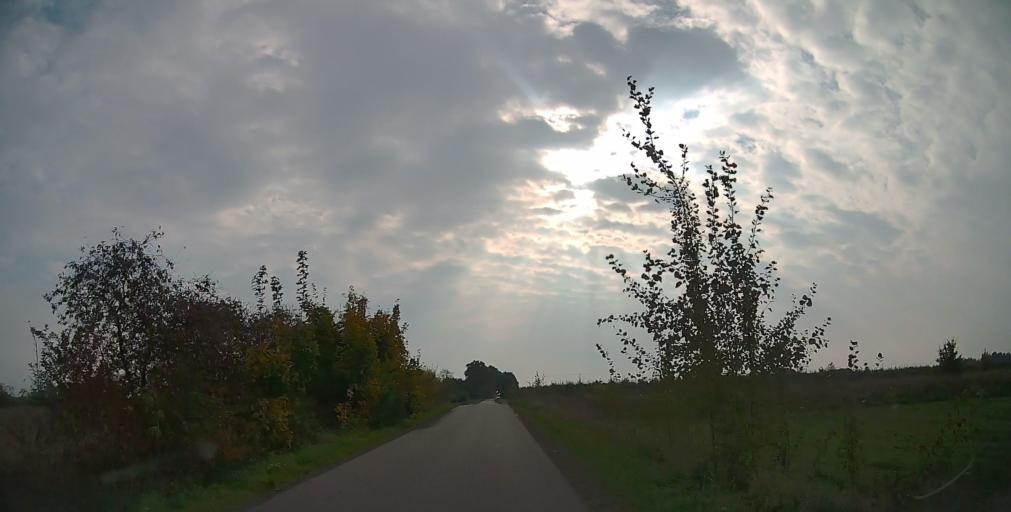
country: PL
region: Masovian Voivodeship
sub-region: Powiat grojecki
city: Mogielnica
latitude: 51.6581
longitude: 20.7153
